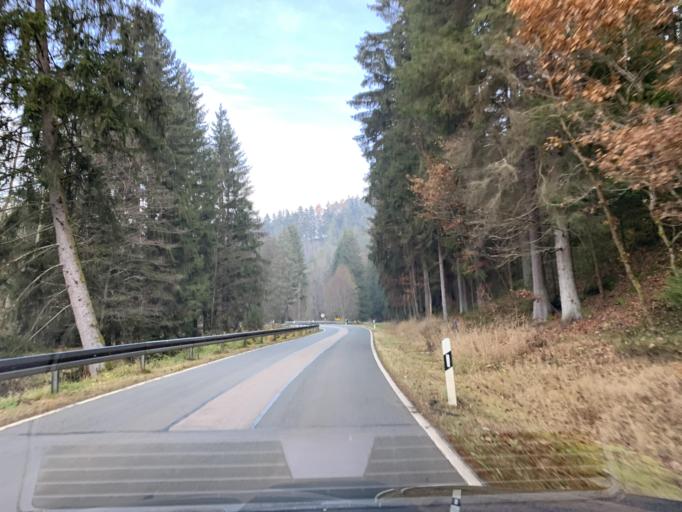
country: DE
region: Bavaria
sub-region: Upper Palatinate
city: Thanstein
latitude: 49.3667
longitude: 12.4315
